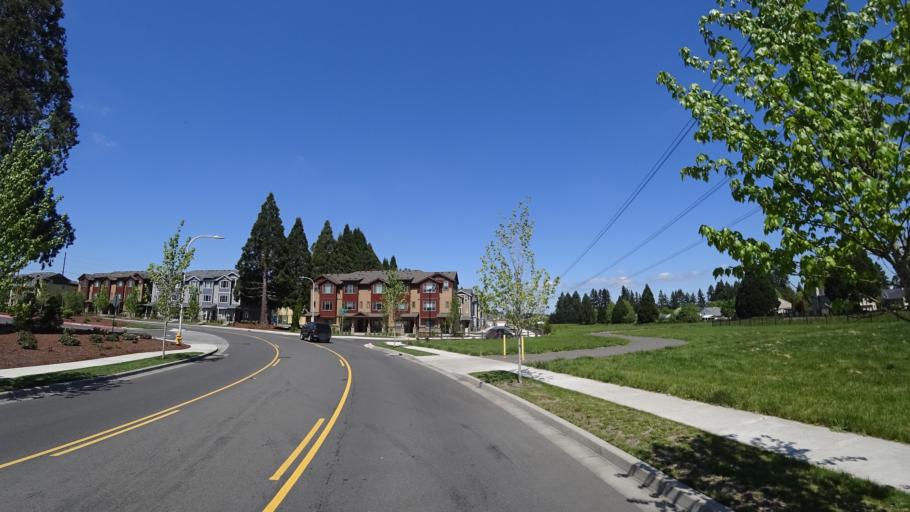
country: US
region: Oregon
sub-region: Washington County
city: Aloha
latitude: 45.5162
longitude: -122.8973
